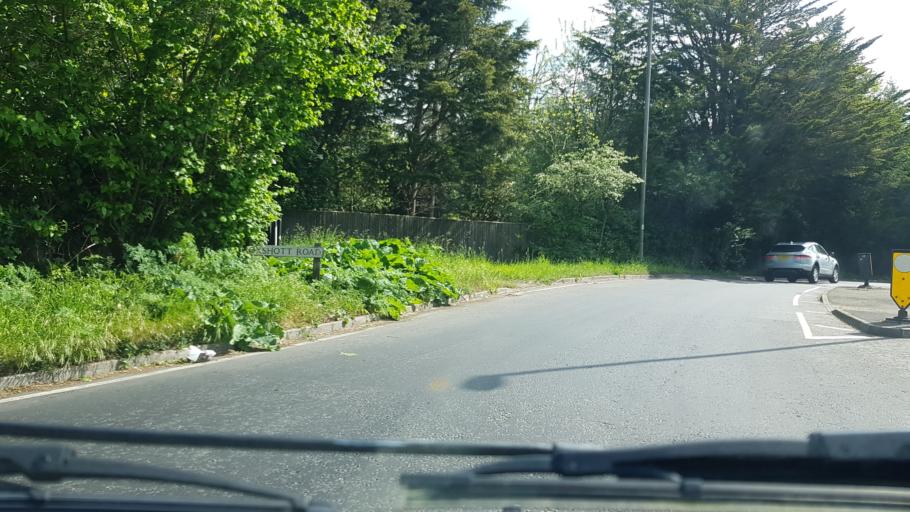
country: GB
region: England
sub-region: Surrey
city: Leatherhead
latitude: 51.3199
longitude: -0.3419
